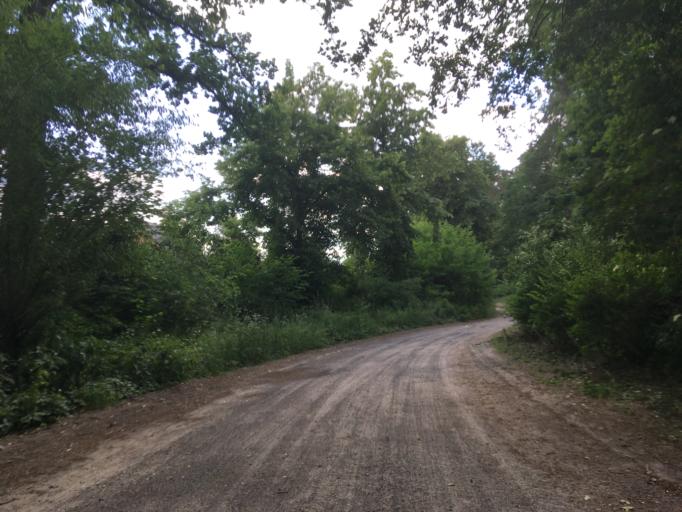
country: DE
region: Brandenburg
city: Muncheberg
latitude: 52.5128
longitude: 14.1062
